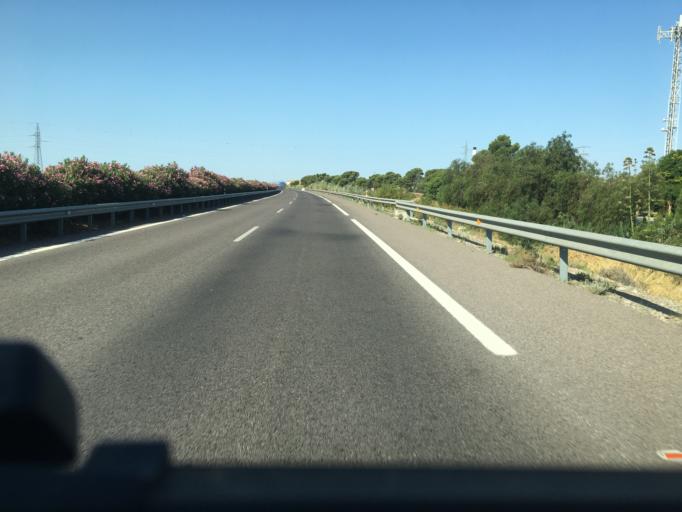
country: ES
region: Murcia
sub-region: Murcia
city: Puerto Lumbreras
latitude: 37.4807
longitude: -1.8692
